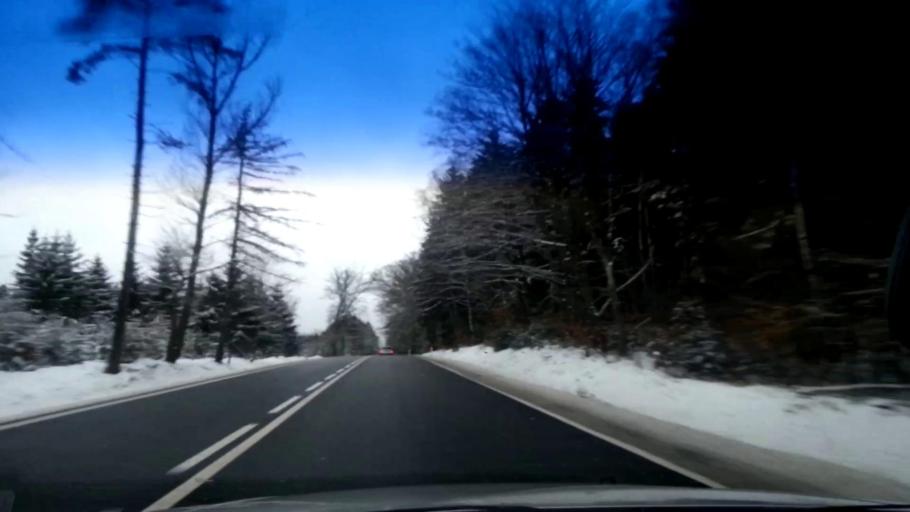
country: CZ
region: Karlovarsky
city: As
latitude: 50.1910
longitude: 12.2276
